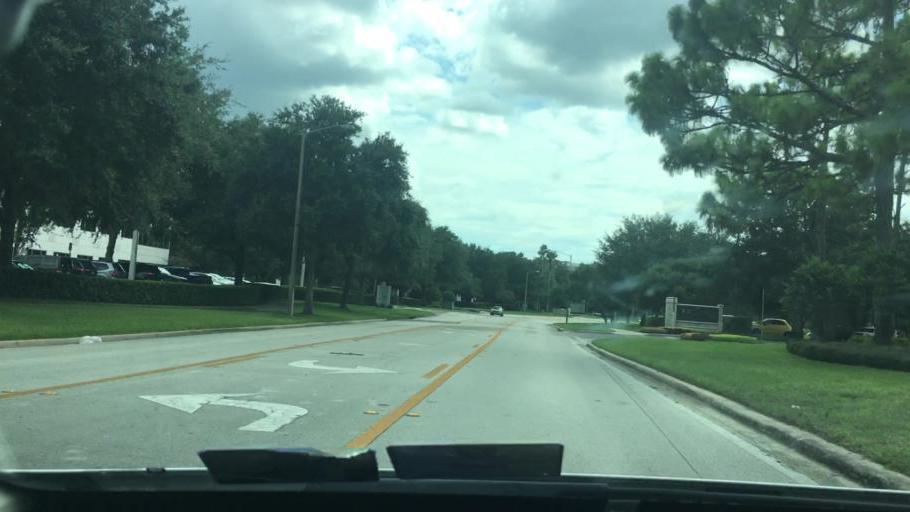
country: US
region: Florida
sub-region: Orange County
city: Alafaya
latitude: 28.6029
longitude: -81.2208
